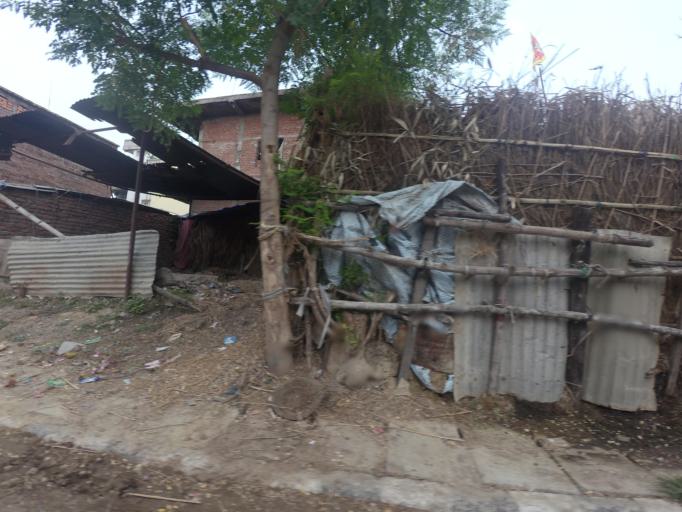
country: NP
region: Western Region
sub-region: Lumbini Zone
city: Bhairahawa
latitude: 27.5105
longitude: 83.4246
